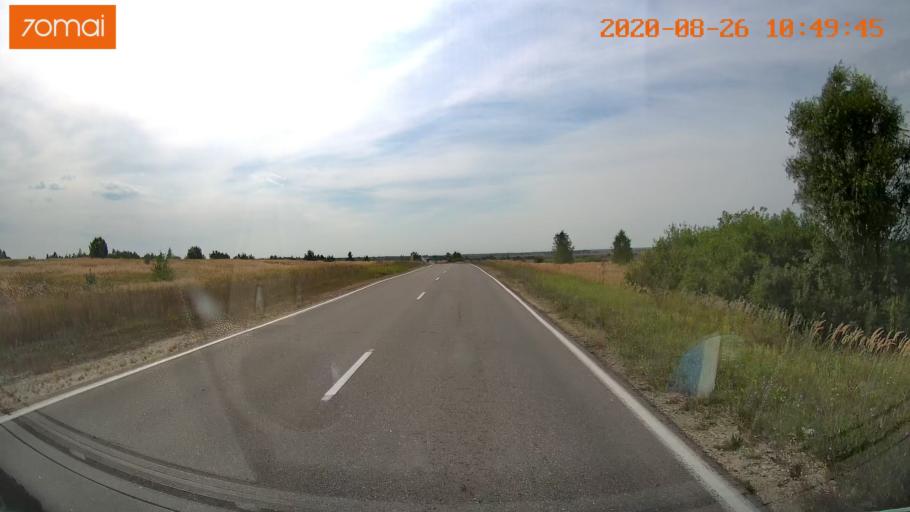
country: RU
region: Rjazan
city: Lashma
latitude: 54.6978
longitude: 41.1581
